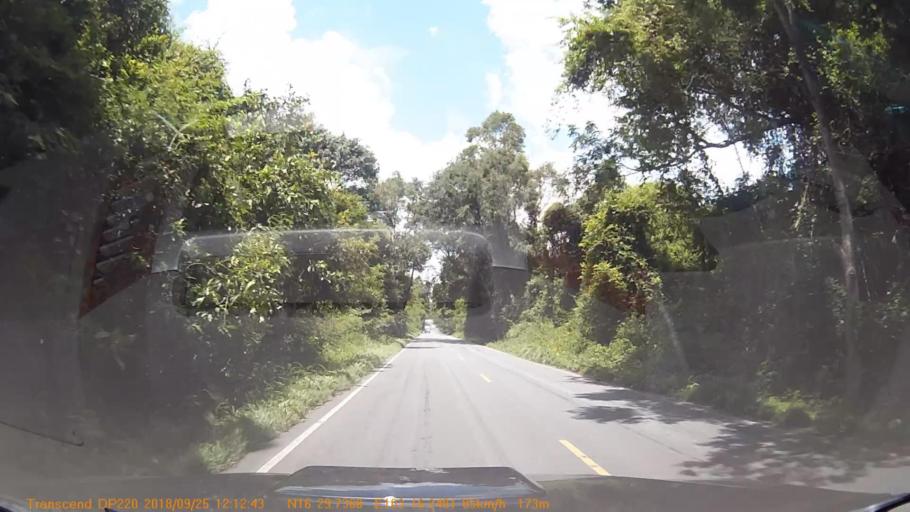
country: TH
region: Kalasin
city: Huai Mek
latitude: 16.4958
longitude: 103.2708
